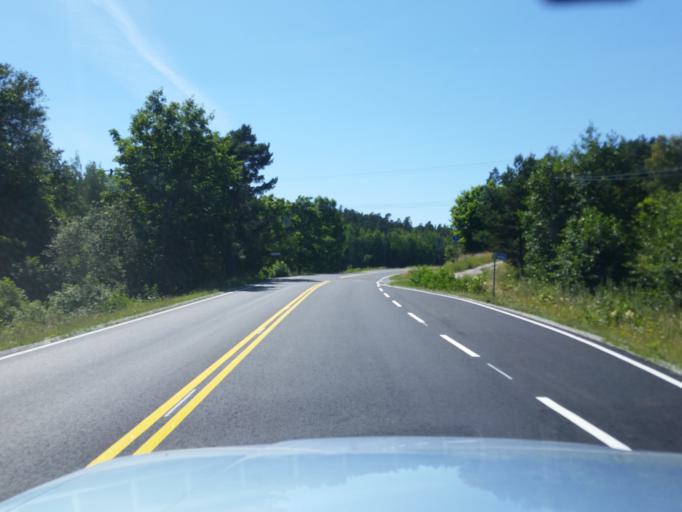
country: FI
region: Varsinais-Suomi
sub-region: Aboland-Turunmaa
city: Laensi-Turunmaa
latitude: 60.2422
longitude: 22.1721
